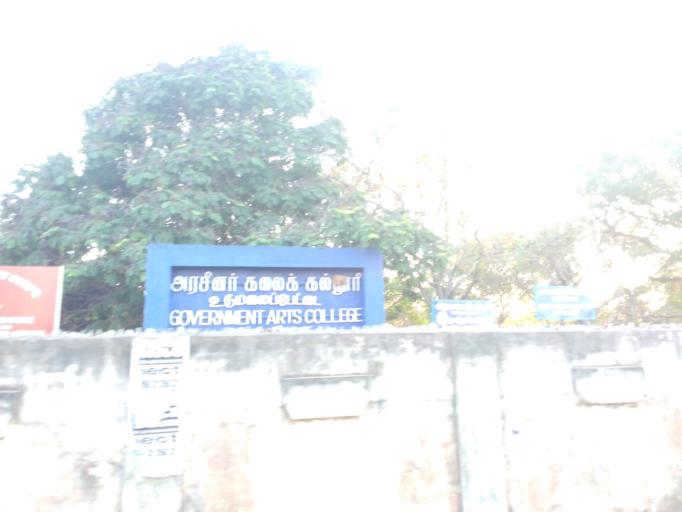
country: IN
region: Tamil Nadu
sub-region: Tiruppur
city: Udumalaippettai
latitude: 10.5667
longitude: 77.2441
